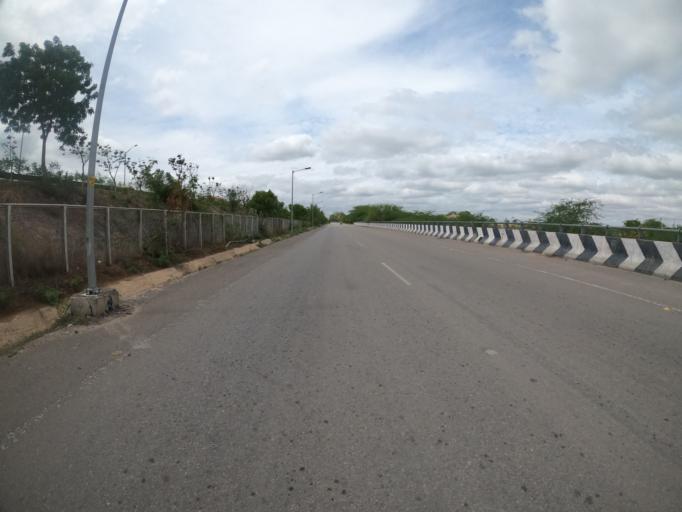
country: IN
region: Telangana
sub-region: Hyderabad
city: Hyderabad
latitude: 17.3034
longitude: 78.3782
